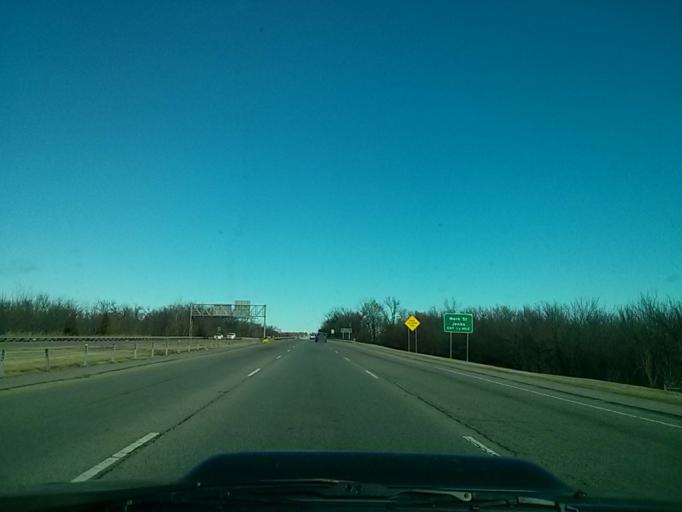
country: US
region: Oklahoma
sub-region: Tulsa County
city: Jenks
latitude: 36.0135
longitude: -96.0115
